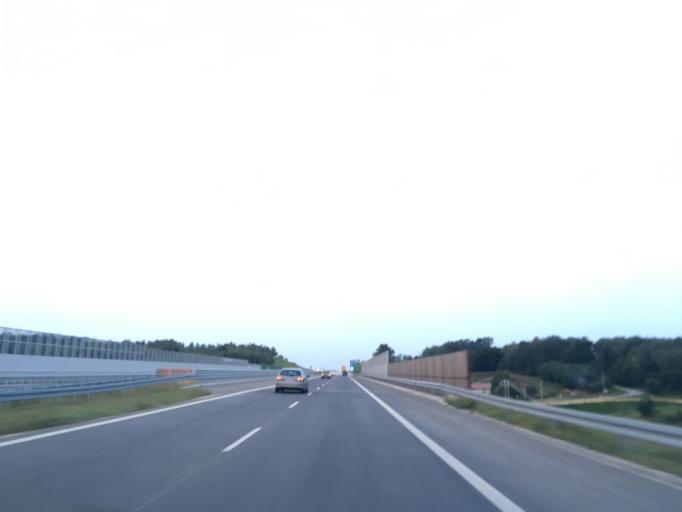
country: PL
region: Lodz Voivodeship
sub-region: Powiat lodzki wschodni
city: Andrespol
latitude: 51.8163
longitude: 19.6408
